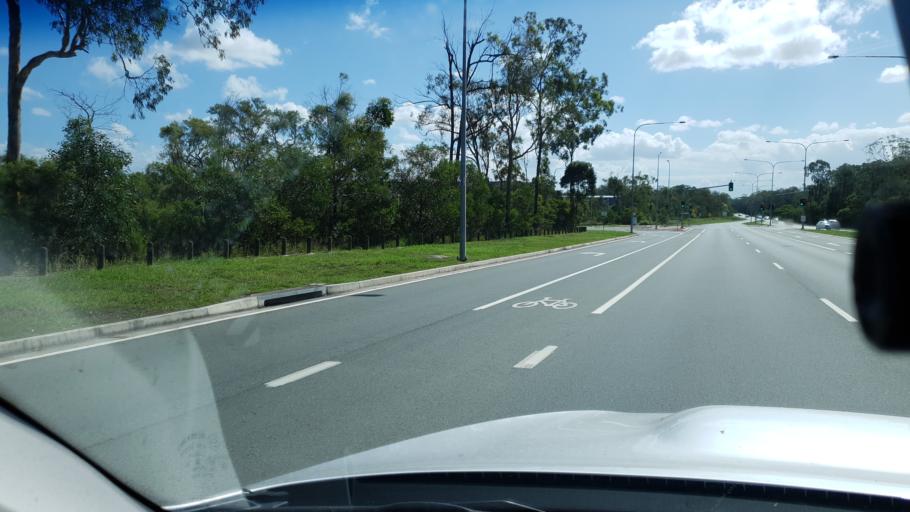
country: AU
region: Queensland
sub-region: Logan
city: Woodridge
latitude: -27.6450
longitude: 153.0956
